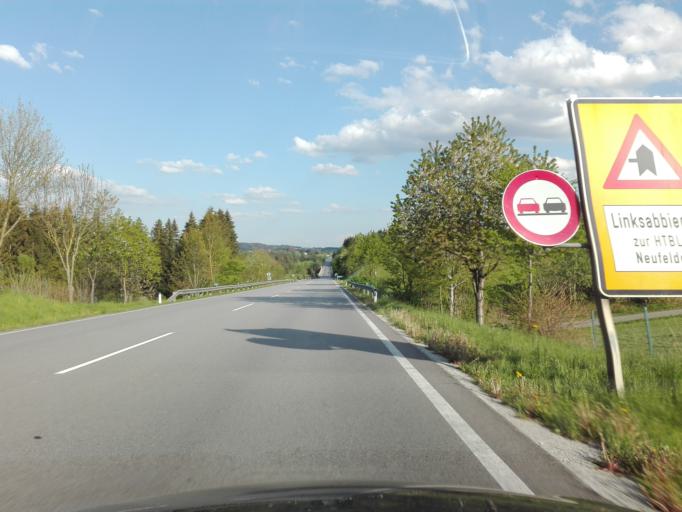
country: AT
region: Upper Austria
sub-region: Politischer Bezirk Rohrbach
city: Kleinzell im Muehlkreis
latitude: 48.4807
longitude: 13.9876
